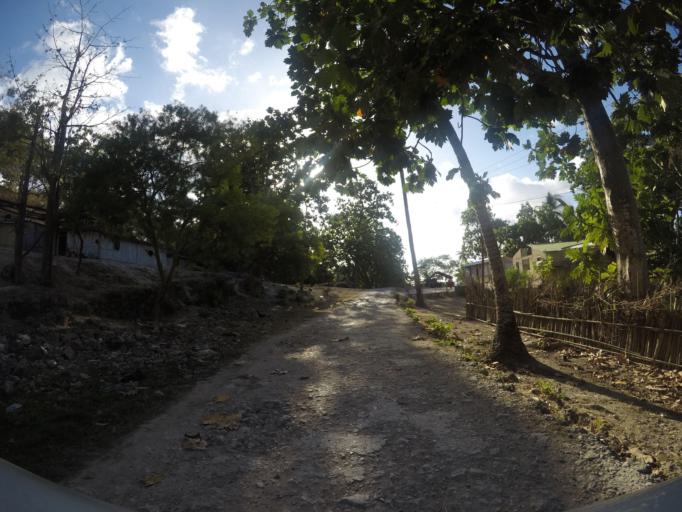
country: TL
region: Lautem
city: Lospalos
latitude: -8.4364
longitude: 126.8510
